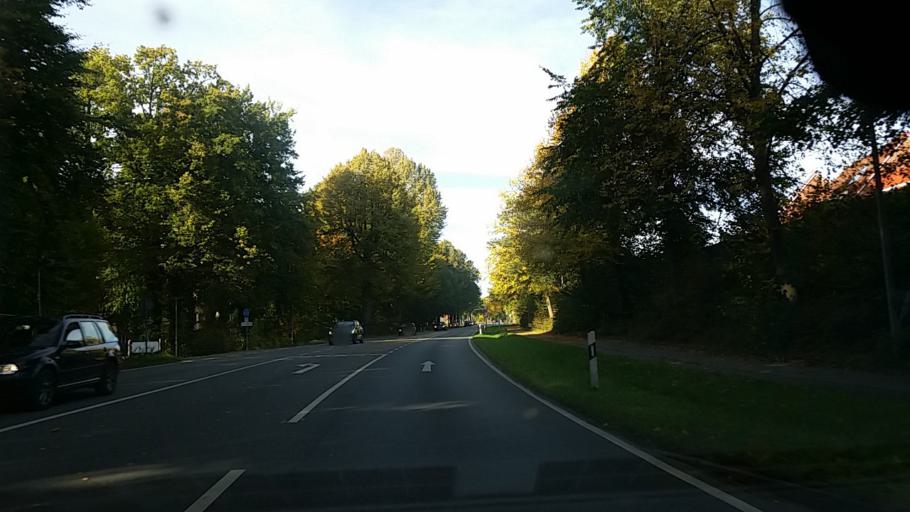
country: DE
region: Schleswig-Holstein
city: Ahrensburg
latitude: 53.6830
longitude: 10.2409
